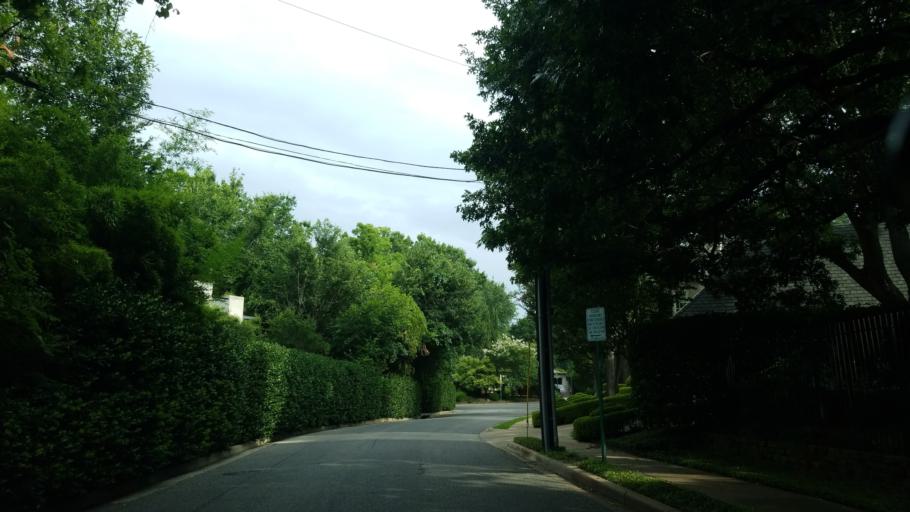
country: US
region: Texas
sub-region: Dallas County
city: University Park
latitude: 32.8414
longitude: -96.8030
